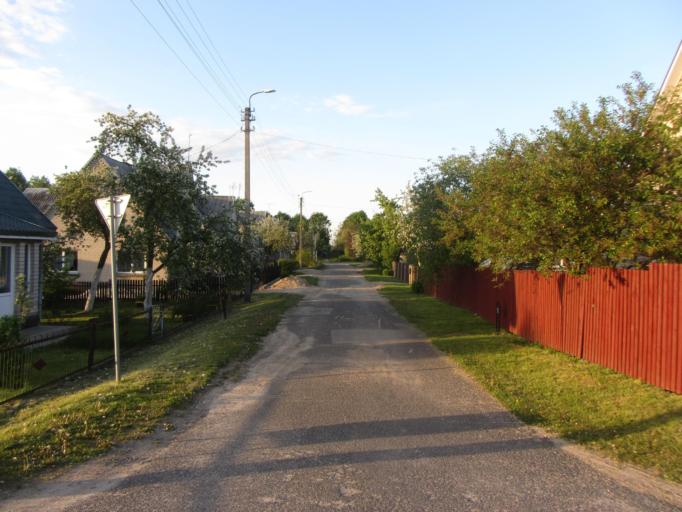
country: LT
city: Sirvintos
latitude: 55.0351
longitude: 24.9669
